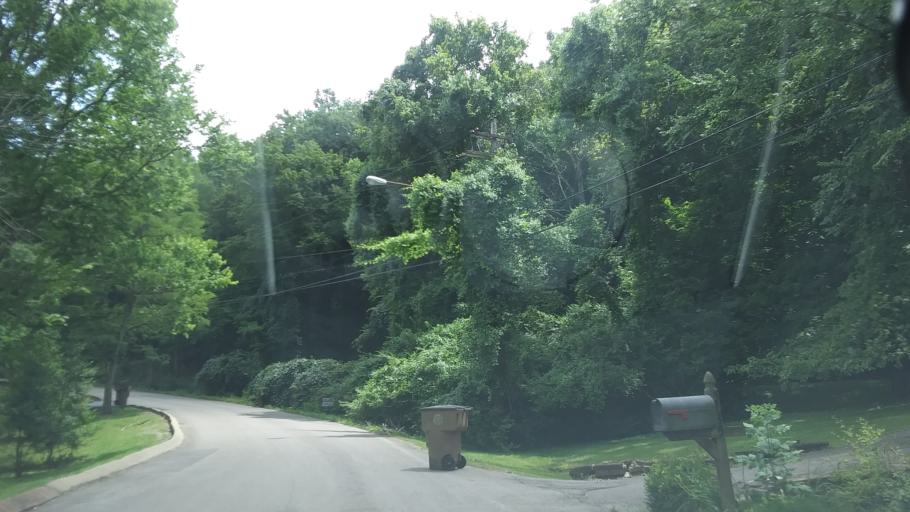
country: US
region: Tennessee
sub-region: Davidson County
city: Belle Meade
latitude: 36.1358
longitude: -86.8707
